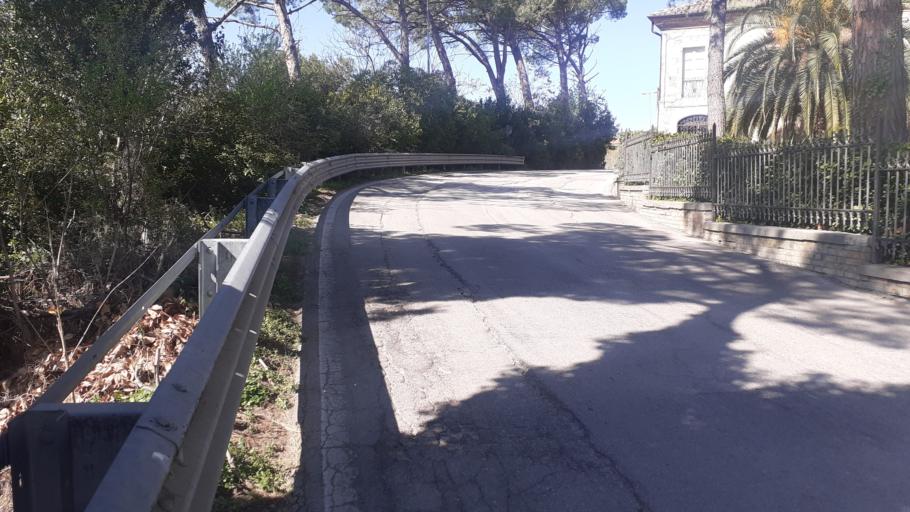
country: IT
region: Abruzzo
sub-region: Provincia di Pescara
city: Cerratina
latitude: 42.3963
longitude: 14.1127
